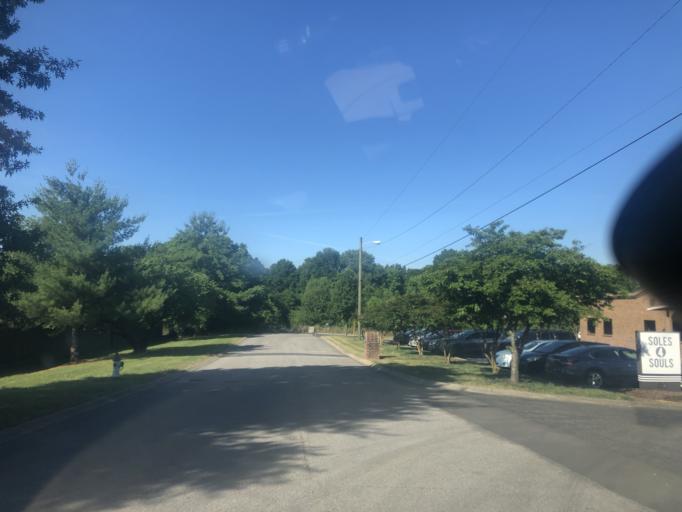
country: US
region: Tennessee
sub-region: Davidson County
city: Lakewood
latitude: 36.2569
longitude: -86.6579
